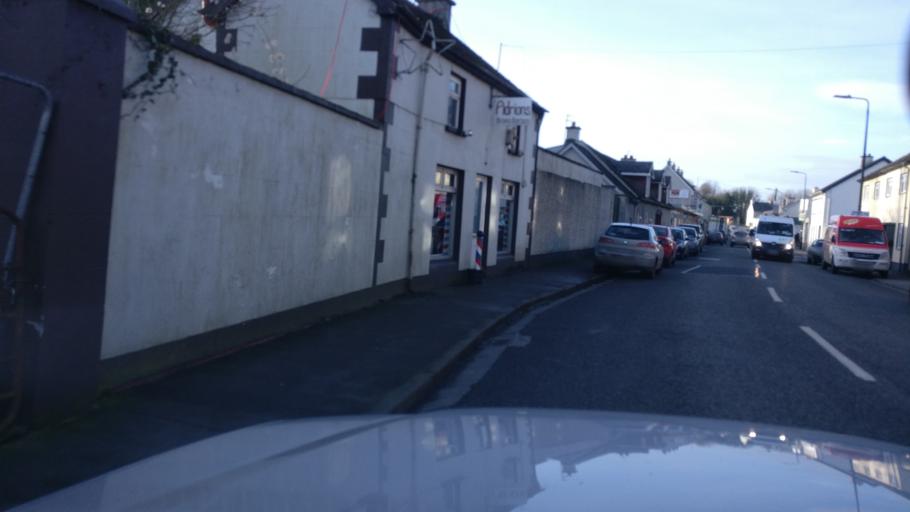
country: IE
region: Leinster
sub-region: Uibh Fhaili
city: Clara
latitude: 53.3416
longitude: -7.6116
